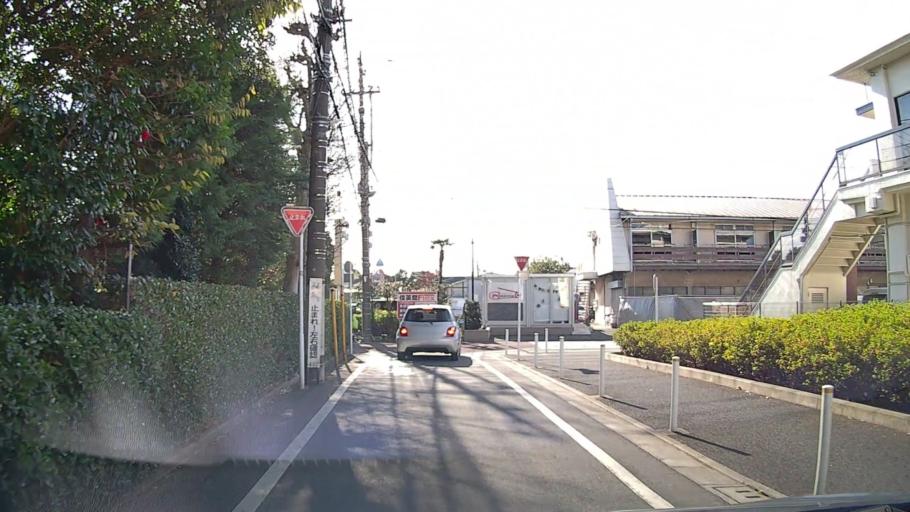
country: JP
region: Saitama
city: Wako
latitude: 35.7539
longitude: 139.6166
